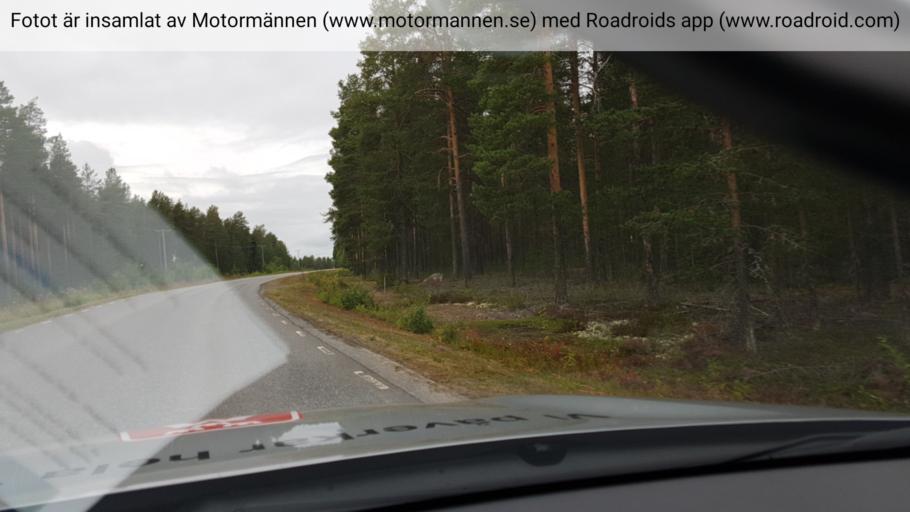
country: SE
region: Norrbotten
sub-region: Bodens Kommun
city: Boden
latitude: 65.8150
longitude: 21.5993
